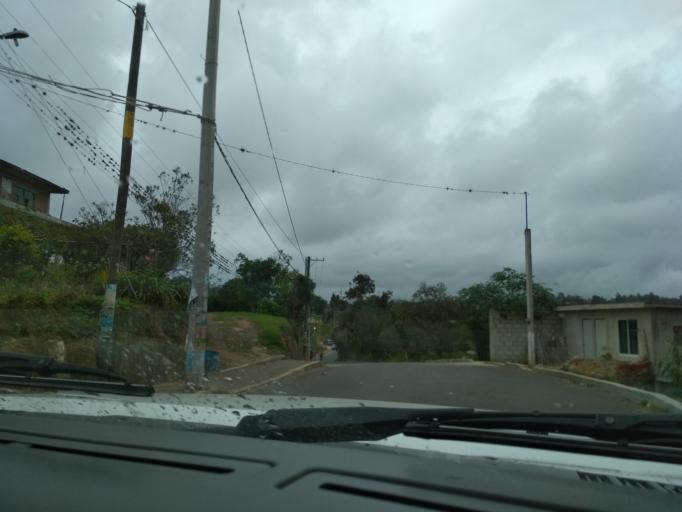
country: MX
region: Veracruz
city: El Castillo
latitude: 19.5382
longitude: -96.8199
